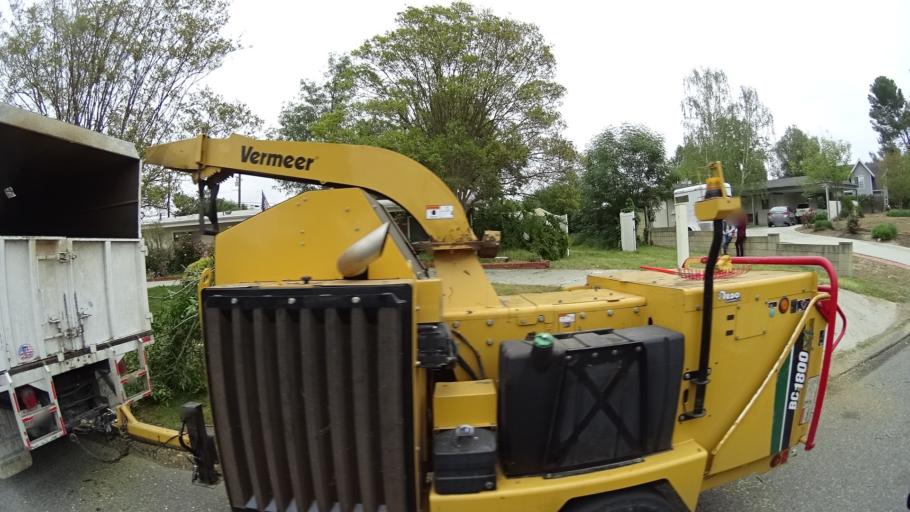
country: US
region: California
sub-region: Ventura County
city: Thousand Oaks
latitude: 34.2027
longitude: -118.8595
